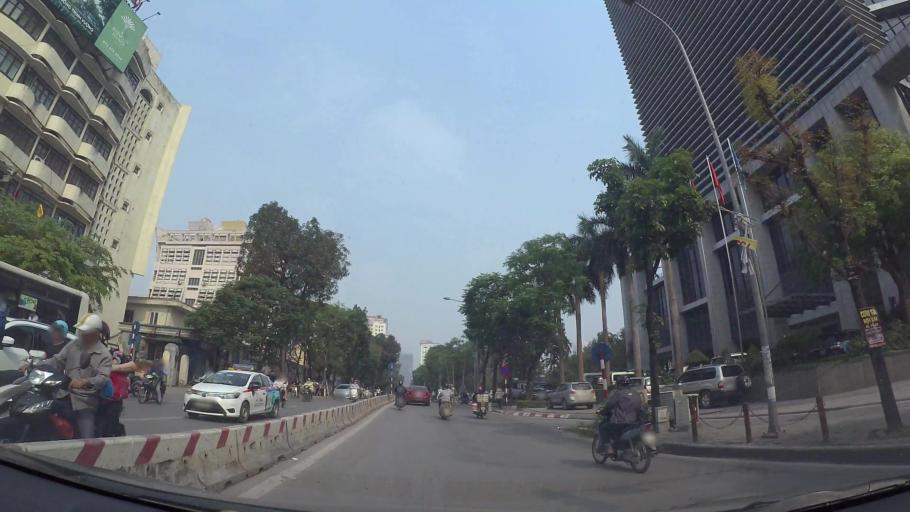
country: VN
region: Ha Noi
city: Dong Da
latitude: 21.0167
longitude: 105.8148
